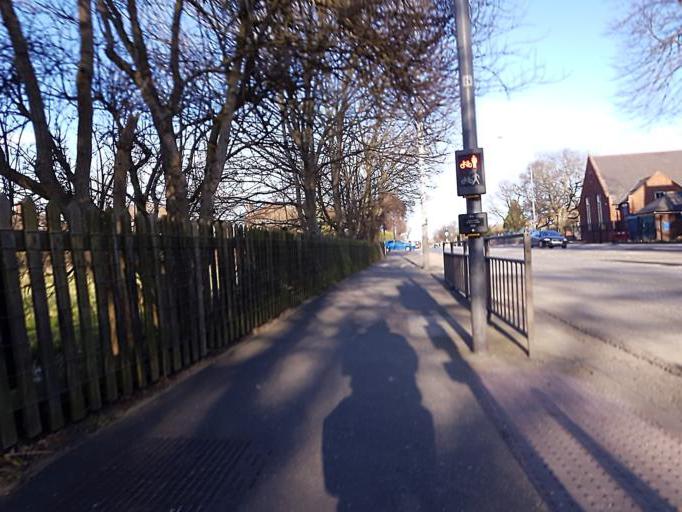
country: GB
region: England
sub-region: North East Lincolnshire
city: Cleethorpes
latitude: 53.5551
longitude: -0.0520
